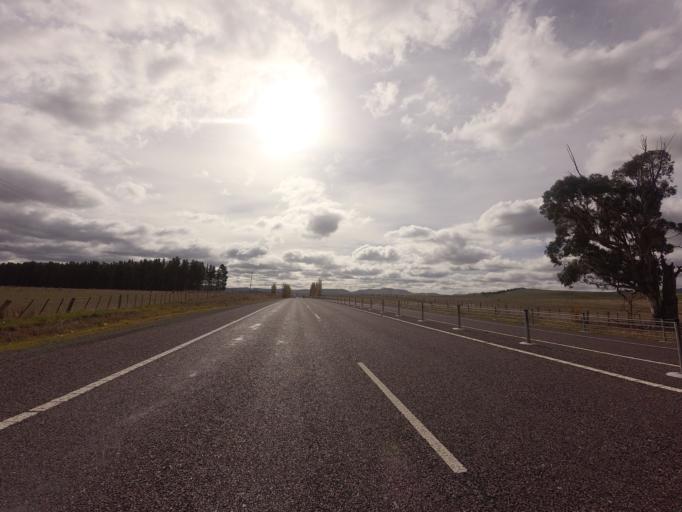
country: AU
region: Tasmania
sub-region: Brighton
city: Bridgewater
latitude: -42.5095
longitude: 147.1885
